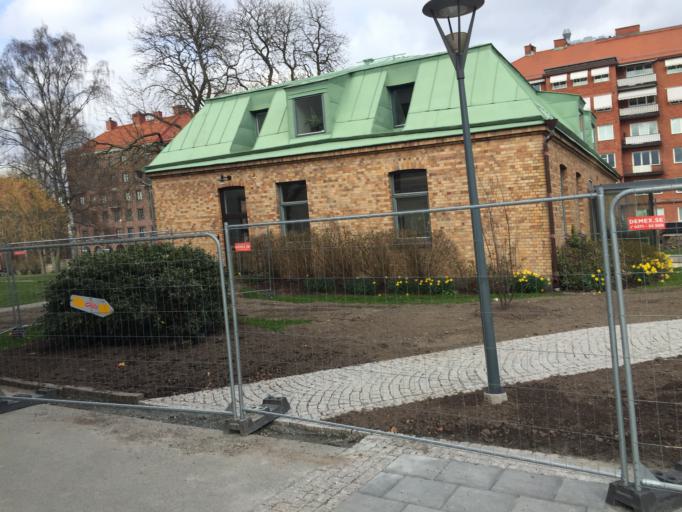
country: SE
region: Vaestra Goetaland
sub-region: Goteborg
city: Goeteborg
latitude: 57.6930
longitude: 11.9759
